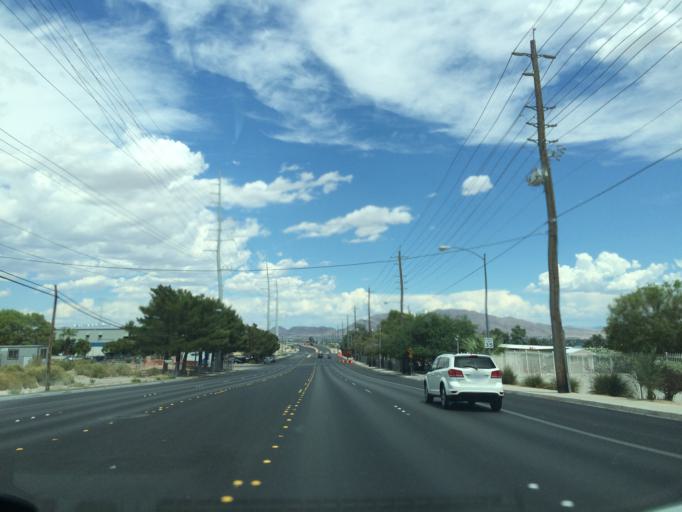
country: US
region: Nevada
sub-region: Clark County
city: North Las Vegas
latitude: 36.2032
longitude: -115.1418
